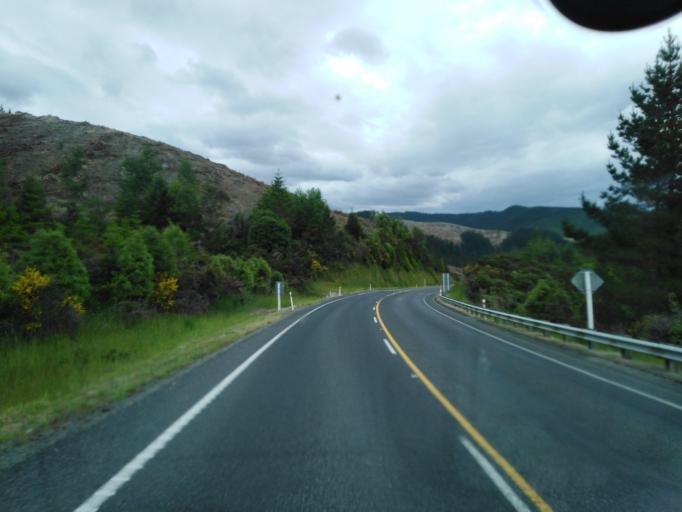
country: NZ
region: Tasman
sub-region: Tasman District
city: Wakefield
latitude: -41.4838
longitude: 172.9057
